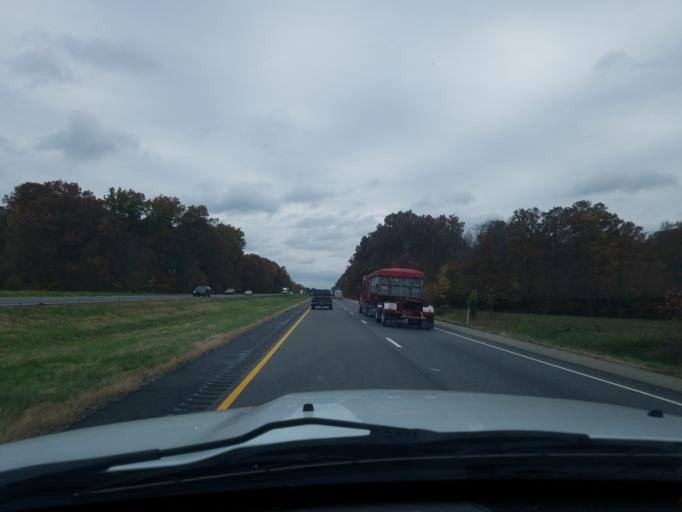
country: US
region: Indiana
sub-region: Jackson County
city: Crothersville
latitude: 38.8062
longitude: -85.8194
